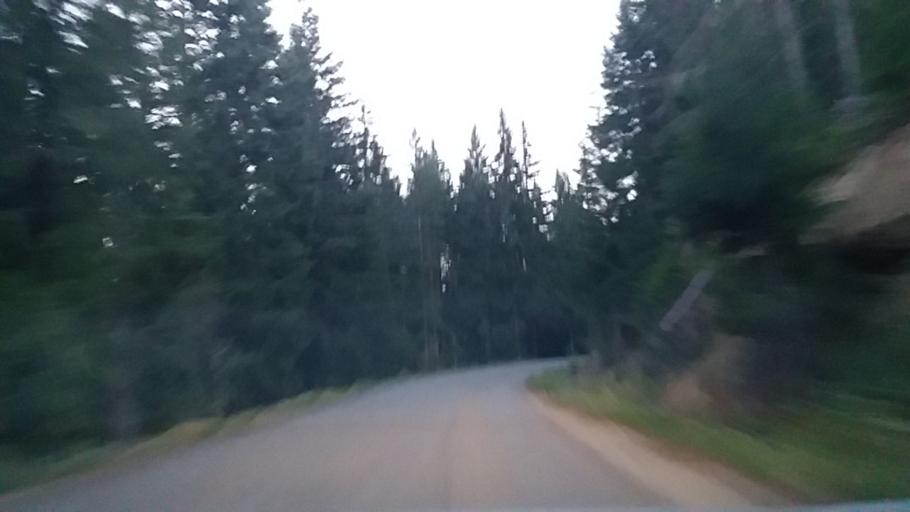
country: US
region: Washington
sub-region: Kittitas County
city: Cle Elum
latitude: 47.3513
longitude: -121.2518
